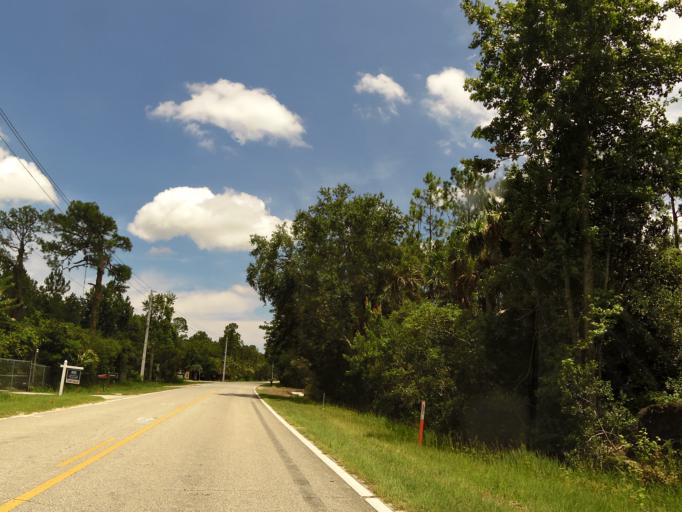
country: US
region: Florida
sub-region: Flagler County
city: Bunnell
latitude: 29.4054
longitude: -81.1891
